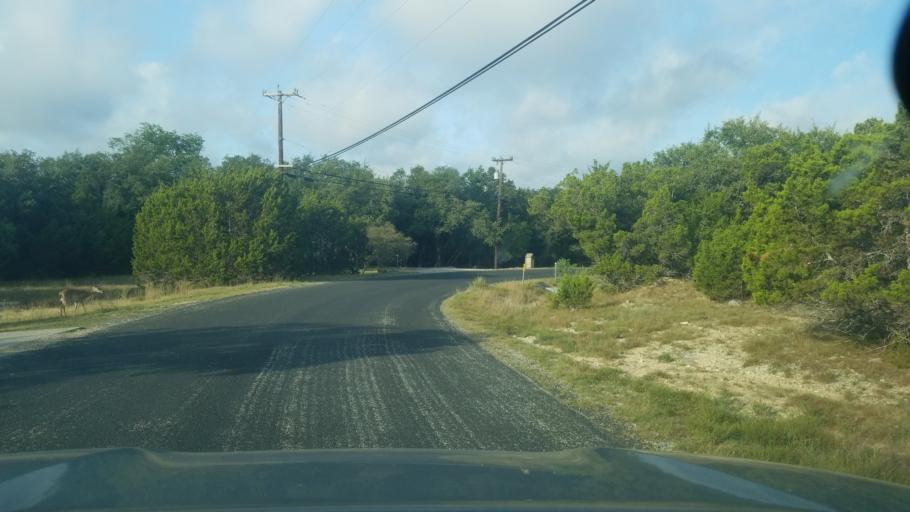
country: US
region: Texas
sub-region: Bexar County
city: Timberwood Park
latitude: 29.6995
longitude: -98.5014
